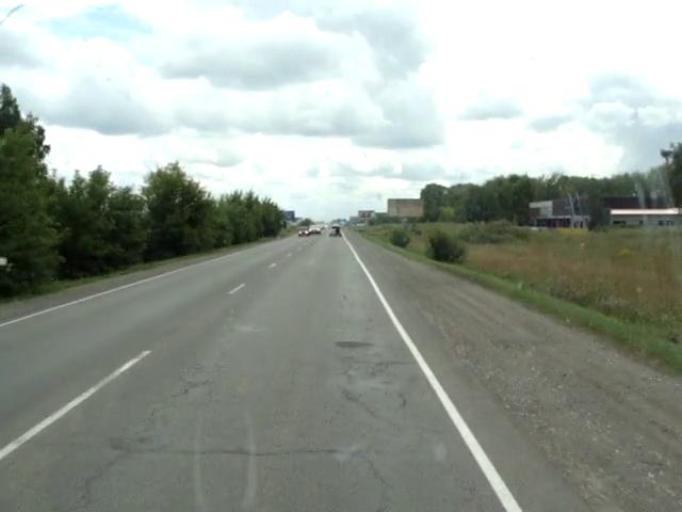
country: RU
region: Altai Krai
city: Zarya
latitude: 52.5738
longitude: 85.1817
